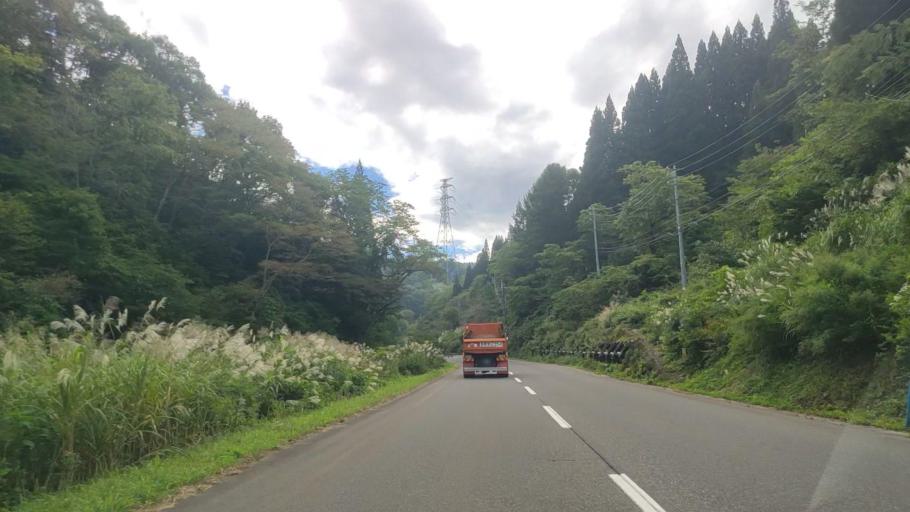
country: JP
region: Nagano
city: Iiyama
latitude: 36.8941
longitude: 138.3217
